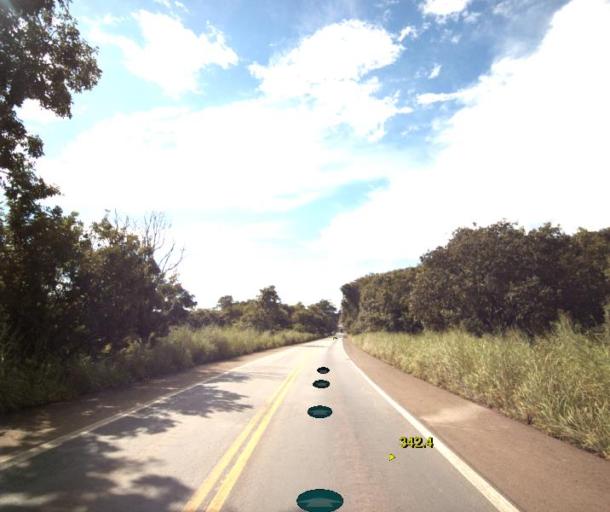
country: BR
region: Goias
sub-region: Jaragua
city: Jaragua
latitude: -15.6075
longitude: -49.4046
